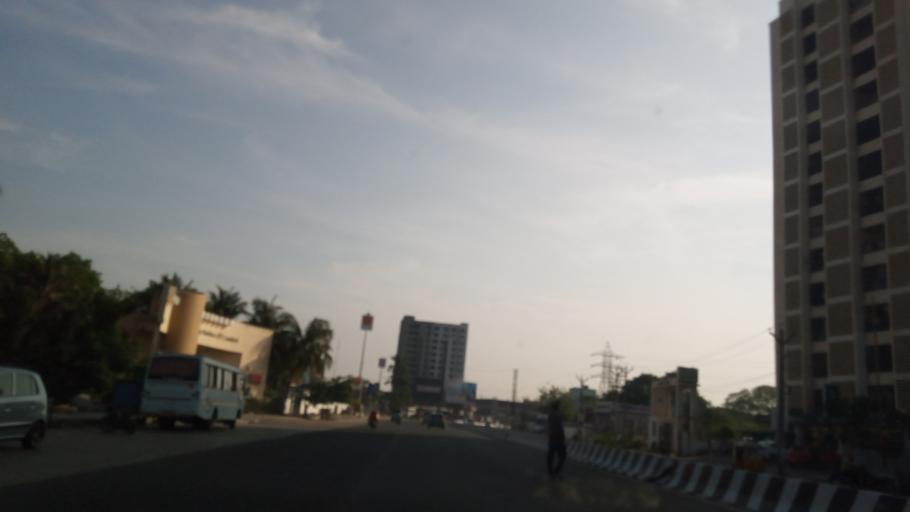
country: IN
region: Tamil Nadu
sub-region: Kancheepuram
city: Poonamalle
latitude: 13.0483
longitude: 80.1206
